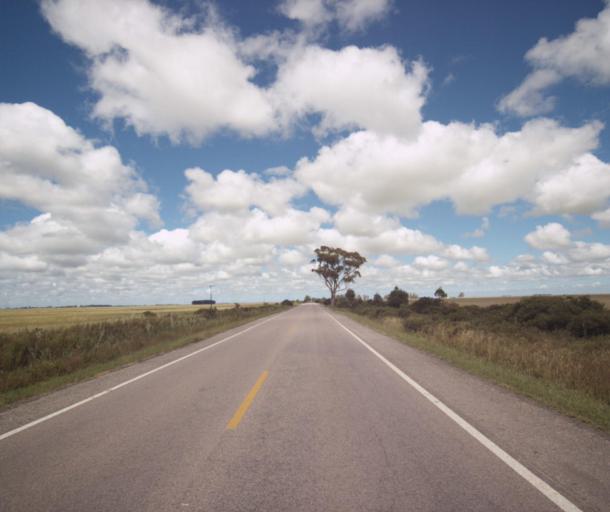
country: BR
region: Rio Grande do Sul
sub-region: Rio Grande
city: Rio Grande
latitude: -32.1722
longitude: -52.4141
